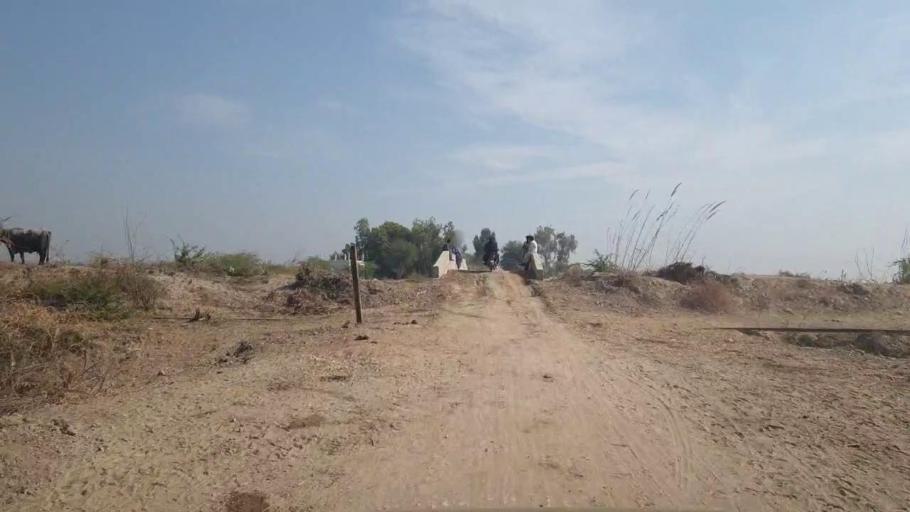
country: PK
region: Sindh
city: Mirwah Gorchani
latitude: 25.3767
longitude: 69.1908
